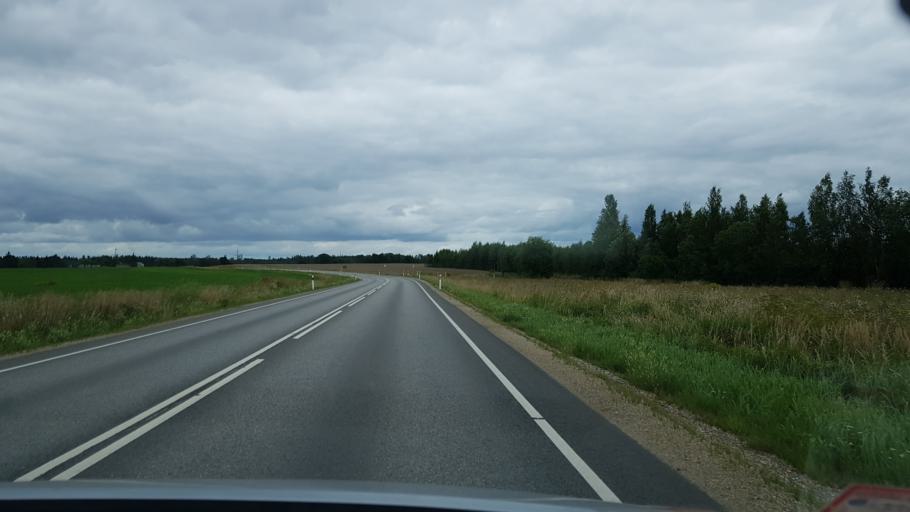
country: EE
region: Polvamaa
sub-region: Polva linn
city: Polva
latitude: 58.0950
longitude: 27.1582
